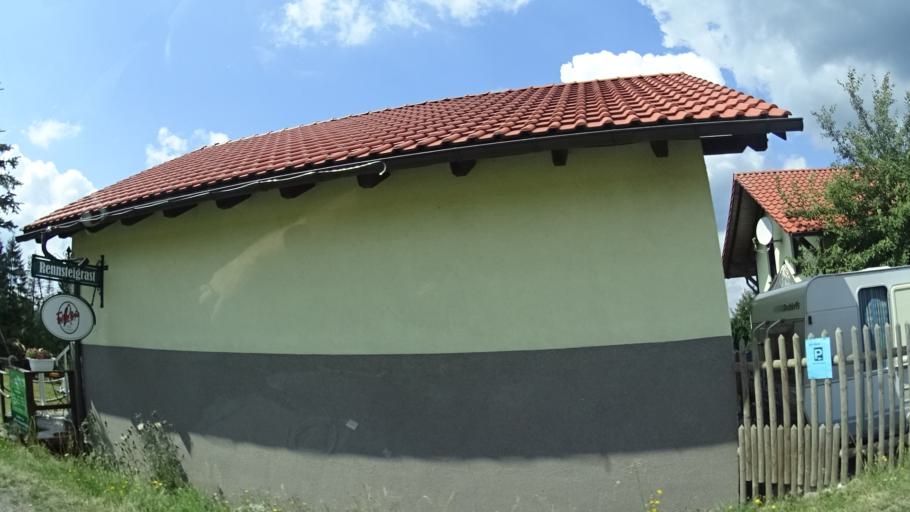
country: DE
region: Thuringia
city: Neustadt am Rennsteig
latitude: 50.5665
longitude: 10.9327
